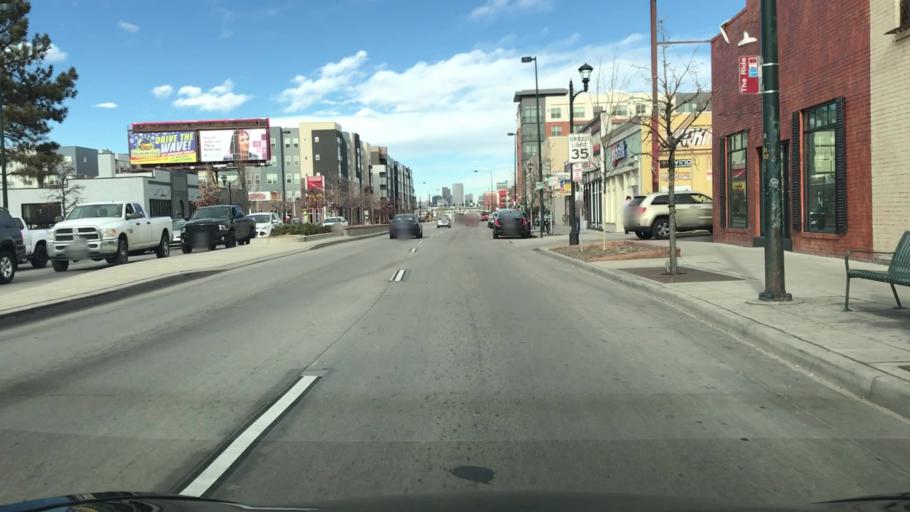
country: US
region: Colorado
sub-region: Arapahoe County
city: Englewood
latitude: 39.6934
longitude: -104.9874
